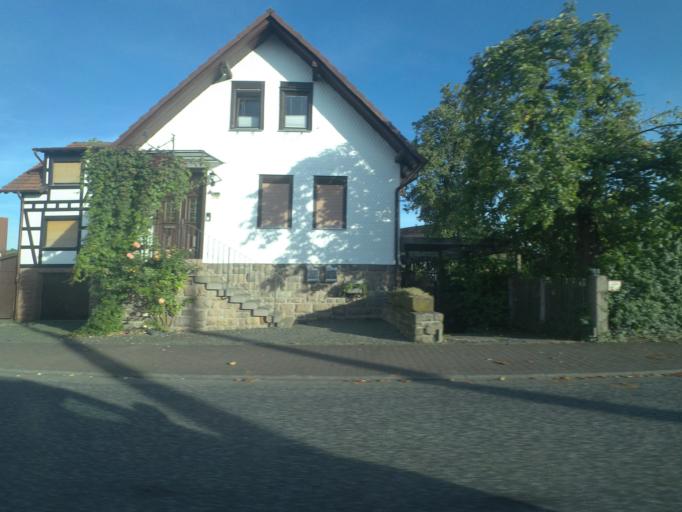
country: DE
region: Hesse
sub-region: Regierungsbezirk Darmstadt
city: Birstein
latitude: 50.3179
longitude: 9.2978
